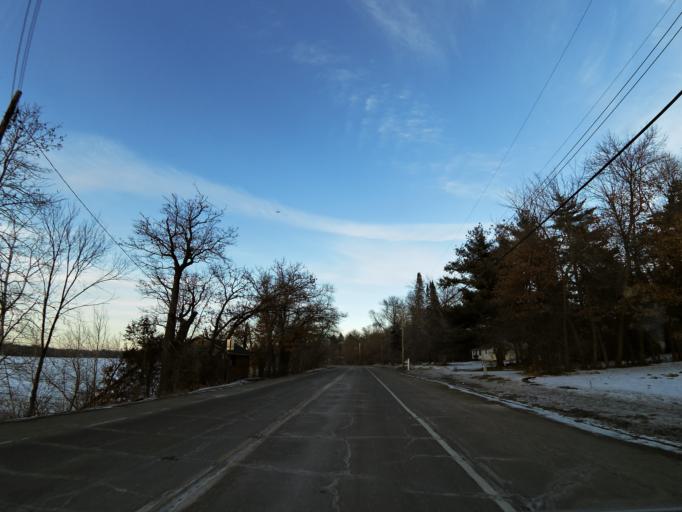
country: US
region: Minnesota
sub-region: Washington County
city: Lake Elmo
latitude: 44.9802
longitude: -92.8821
